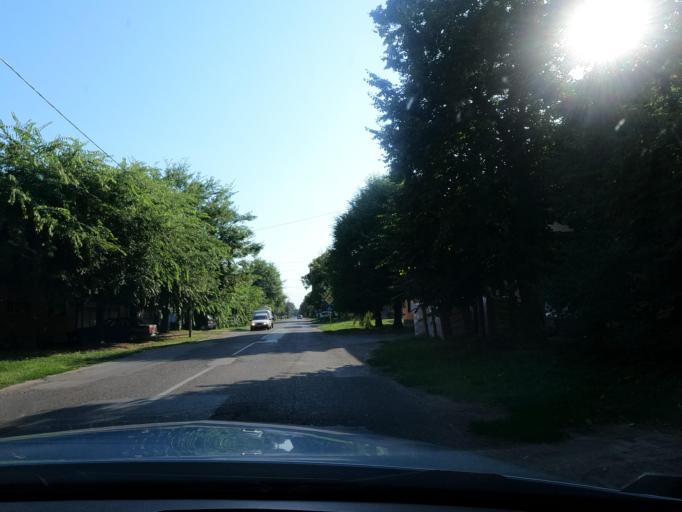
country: RS
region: Autonomna Pokrajina Vojvodina
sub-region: Juznobacki Okrug
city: Becej
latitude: 45.6100
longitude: 20.0414
